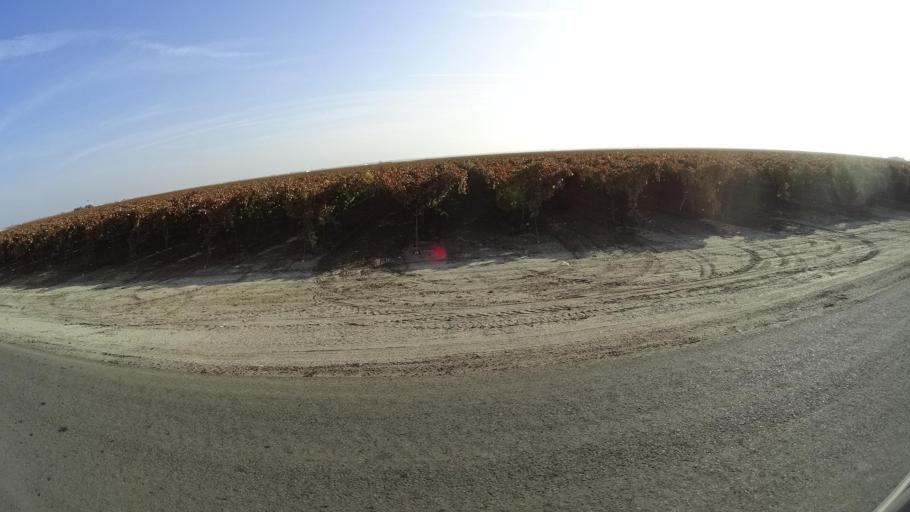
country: US
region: California
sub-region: Kern County
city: McFarland
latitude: 35.7103
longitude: -119.1872
